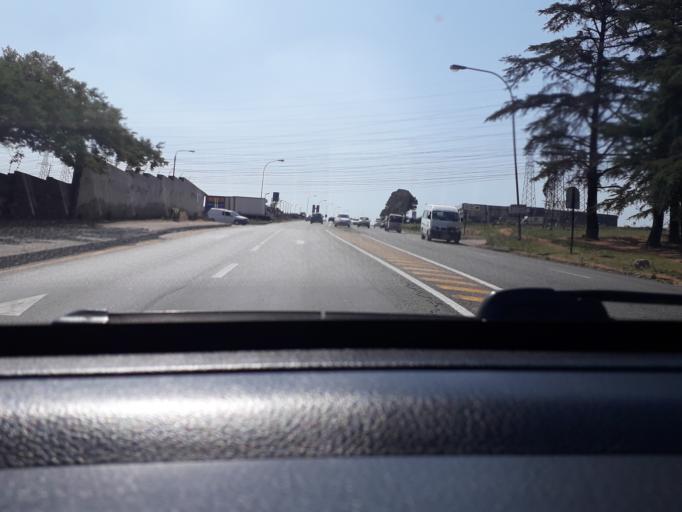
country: ZA
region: Gauteng
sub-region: City of Johannesburg Metropolitan Municipality
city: Modderfontein
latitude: -26.1260
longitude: 28.1429
